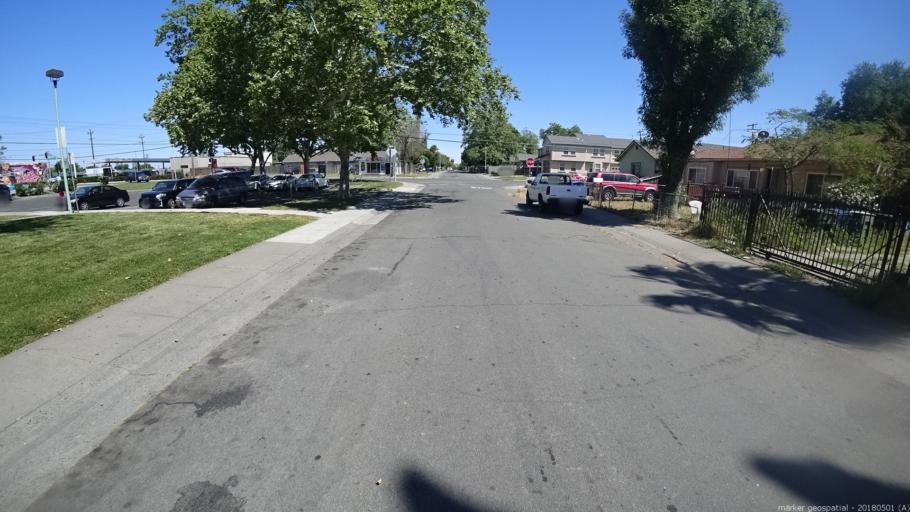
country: US
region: California
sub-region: Sacramento County
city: Rio Linda
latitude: 38.6362
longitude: -121.4450
